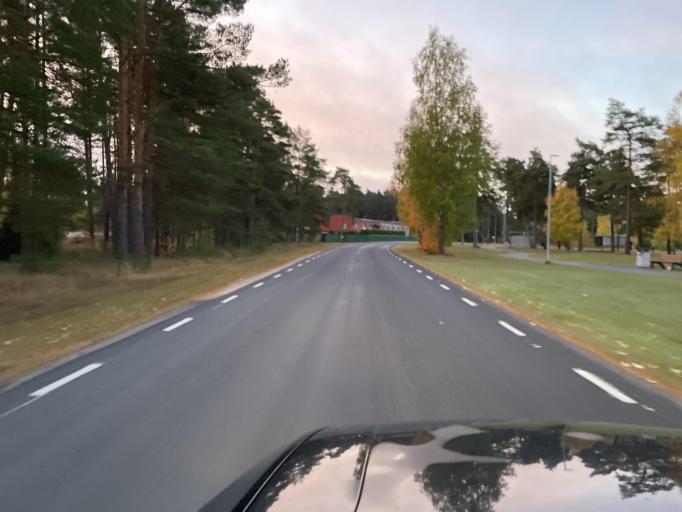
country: EE
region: Harju
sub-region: Nissi vald
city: Riisipere
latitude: 59.2478
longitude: 24.2410
